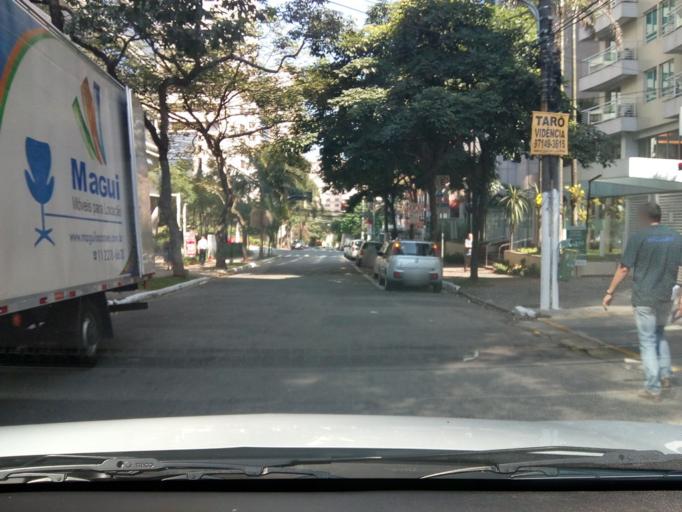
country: BR
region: Sao Paulo
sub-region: Sao Paulo
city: Sao Paulo
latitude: -23.5707
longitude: -46.6460
